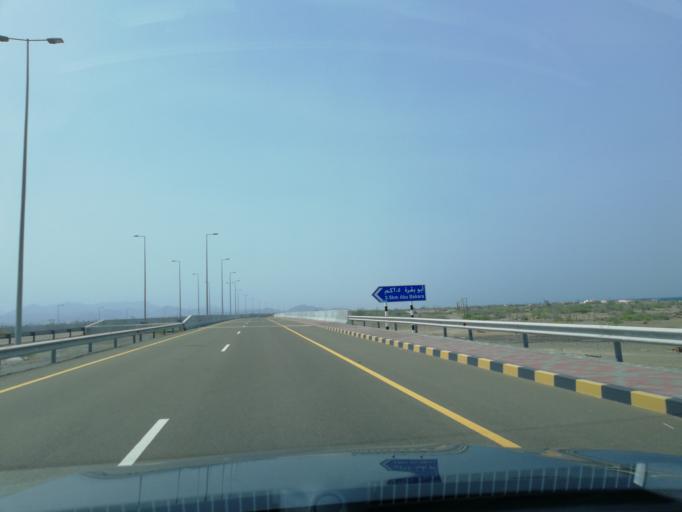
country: OM
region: Al Batinah
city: Shinas
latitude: 24.8685
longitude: 56.4097
